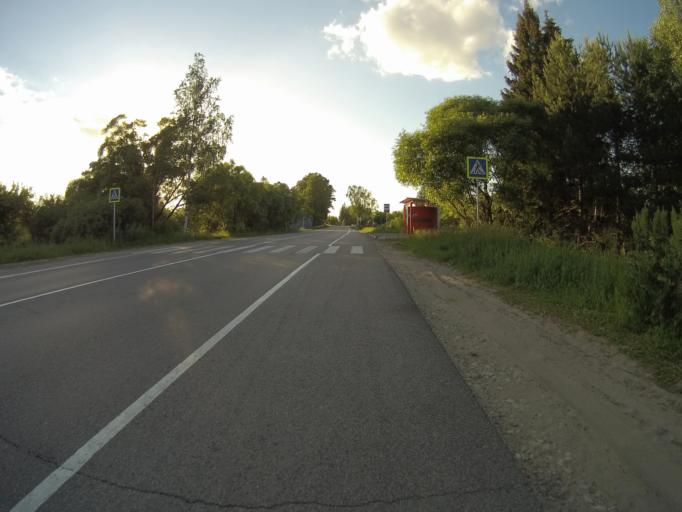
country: RU
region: Vladimir
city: Golovino
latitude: 55.9279
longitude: 40.5974
